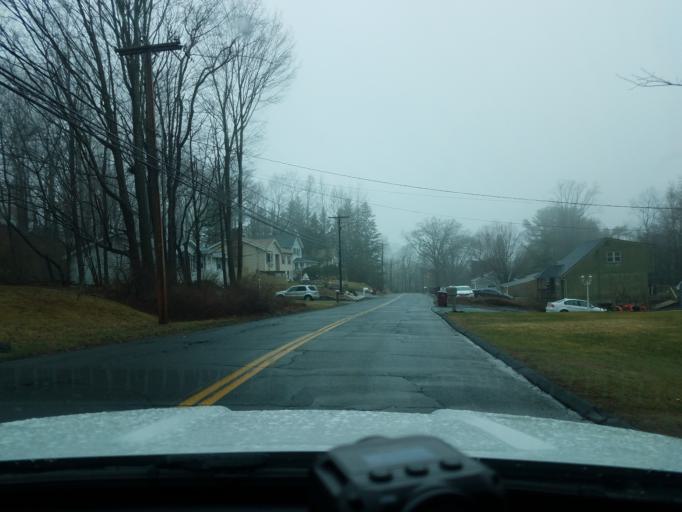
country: US
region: Connecticut
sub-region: New Haven County
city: Naugatuck
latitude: 41.4876
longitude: -73.0386
